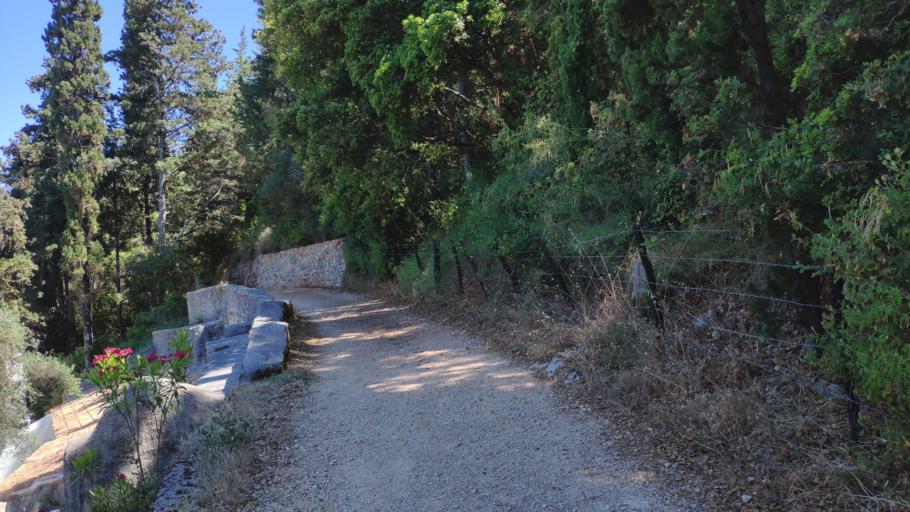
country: GR
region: Ionian Islands
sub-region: Lefkada
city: Lefkada
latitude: 38.8316
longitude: 20.6669
